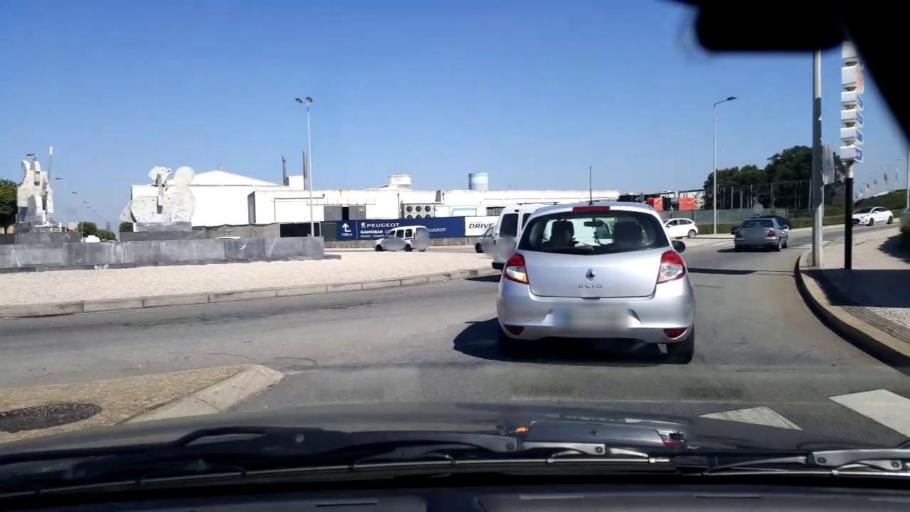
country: PT
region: Porto
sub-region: Vila do Conde
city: Vila do Conde
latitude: 41.3602
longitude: -8.7445
